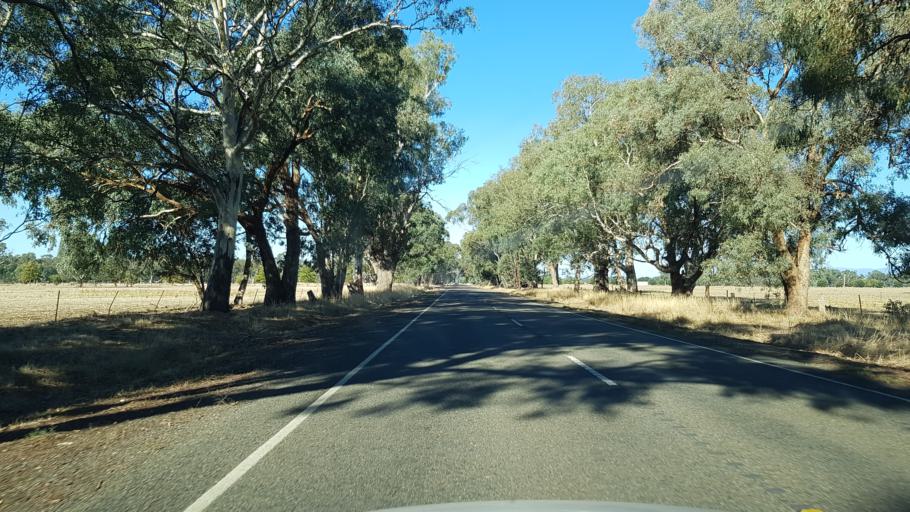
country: AU
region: Victoria
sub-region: Wangaratta
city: Wangaratta
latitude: -36.4371
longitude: 146.3356
